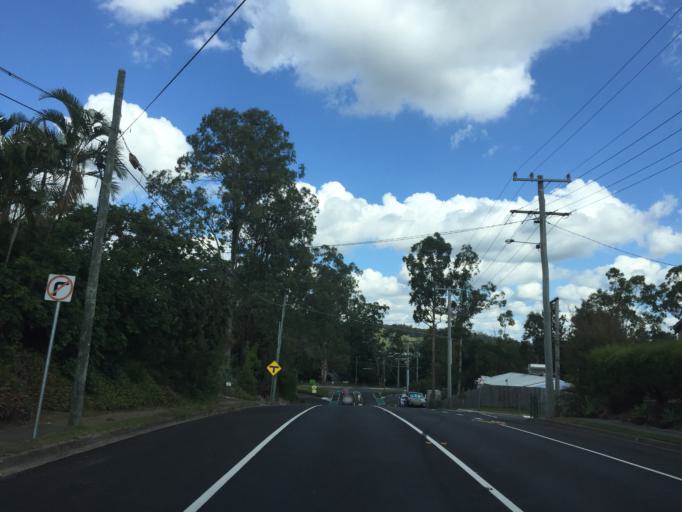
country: AU
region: Queensland
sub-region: Moreton Bay
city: Ferny Hills
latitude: -27.3990
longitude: 152.9374
